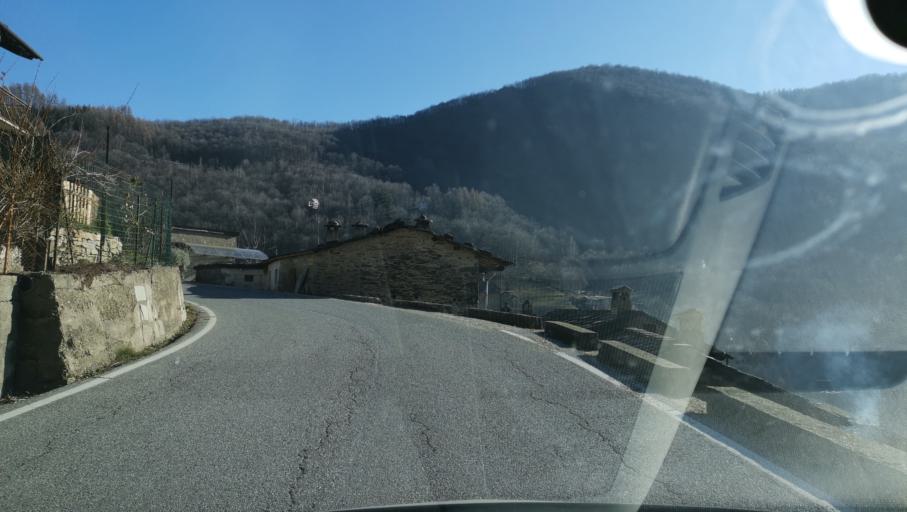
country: IT
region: Piedmont
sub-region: Provincia di Torino
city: Rora
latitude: 44.7902
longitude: 7.2096
